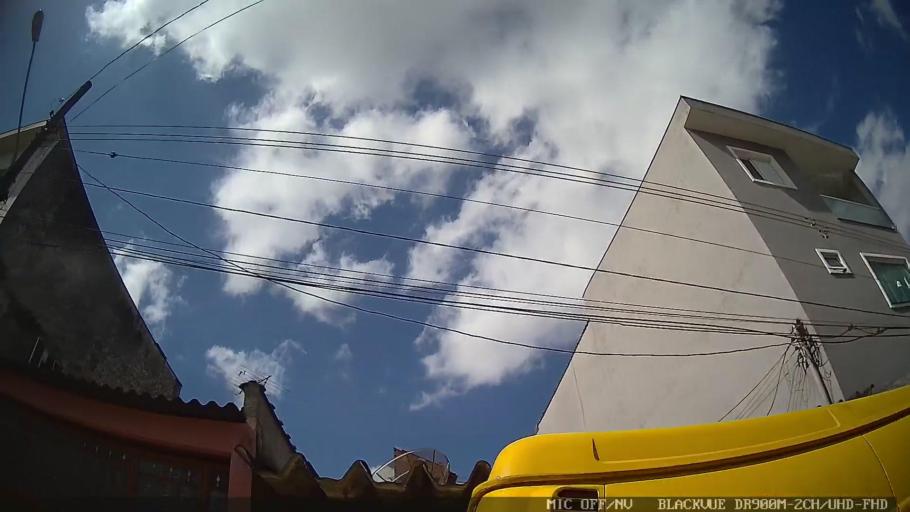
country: BR
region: Sao Paulo
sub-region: Sao Caetano Do Sul
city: Sao Caetano do Sul
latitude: -23.6276
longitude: -46.5879
